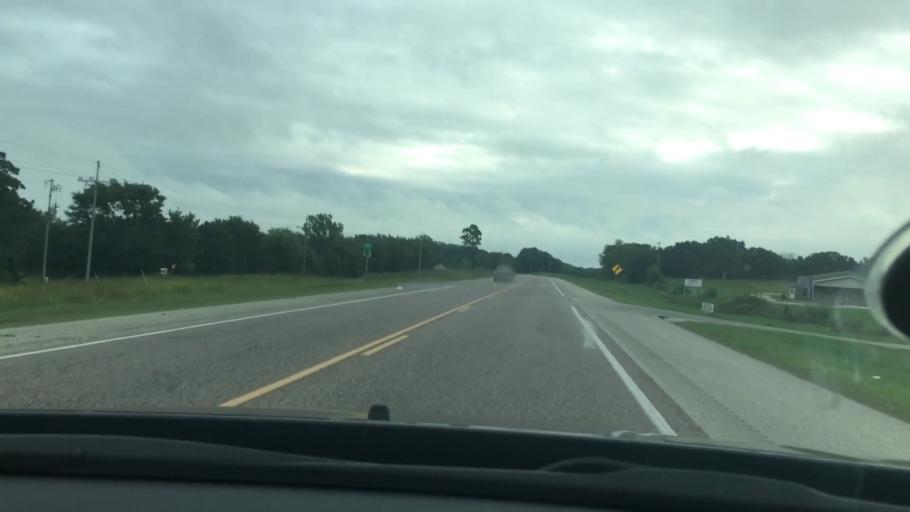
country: US
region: Oklahoma
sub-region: Pontotoc County
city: Ada
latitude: 34.7980
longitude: -96.5481
